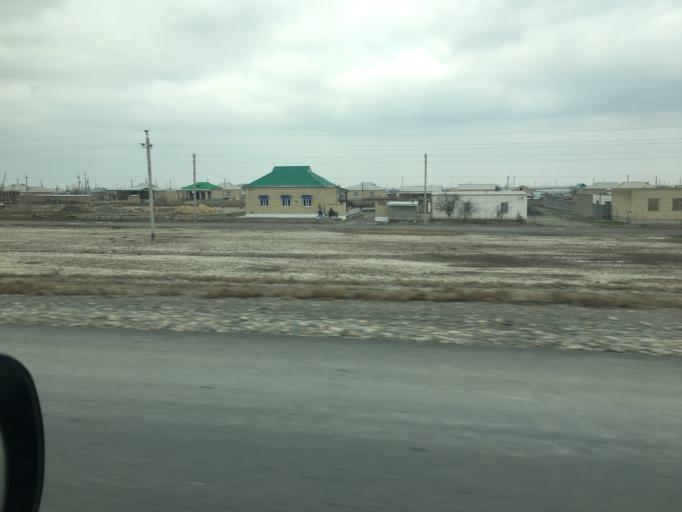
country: TM
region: Ahal
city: Kaka
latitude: 37.2973
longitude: 59.7781
